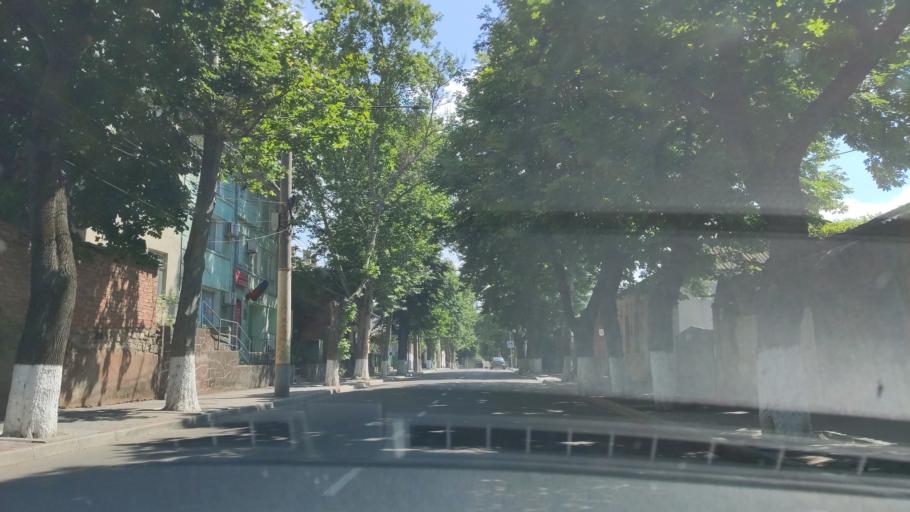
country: MD
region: Raionul Soroca
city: Soroca
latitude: 48.1526
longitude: 28.3001
